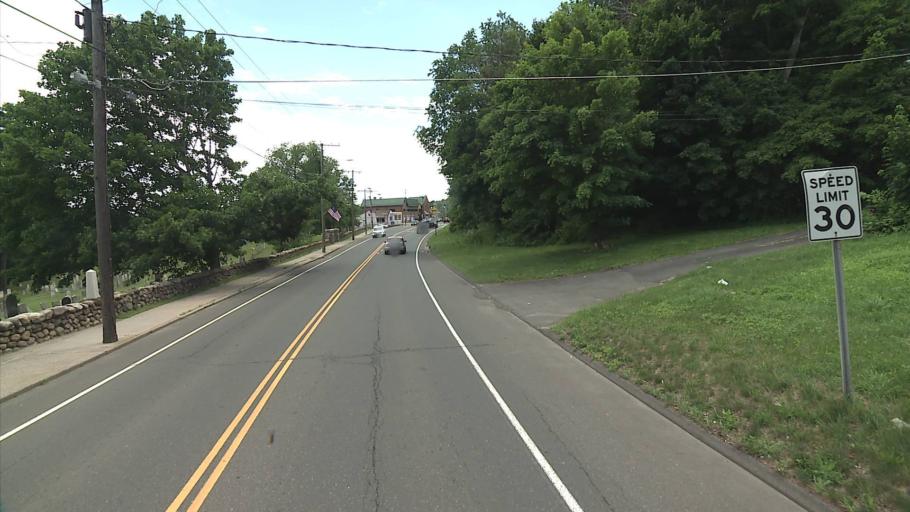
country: US
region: Connecticut
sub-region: Litchfield County
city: Watertown
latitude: 41.5998
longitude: -73.1143
